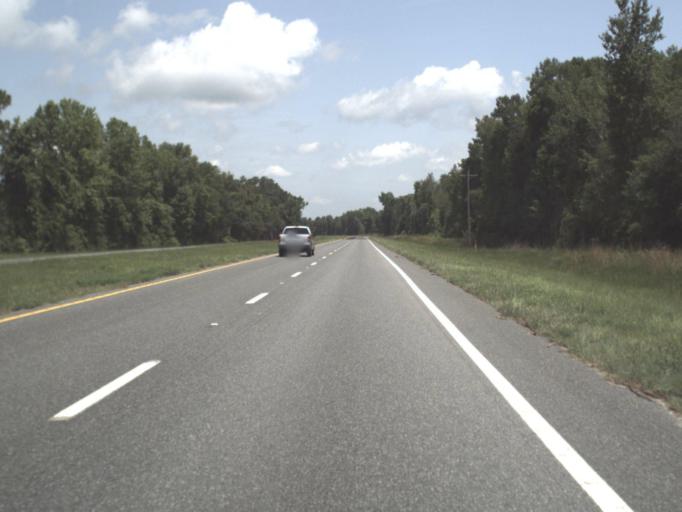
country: US
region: Florida
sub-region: Taylor County
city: Perry
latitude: 29.9395
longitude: -83.4482
